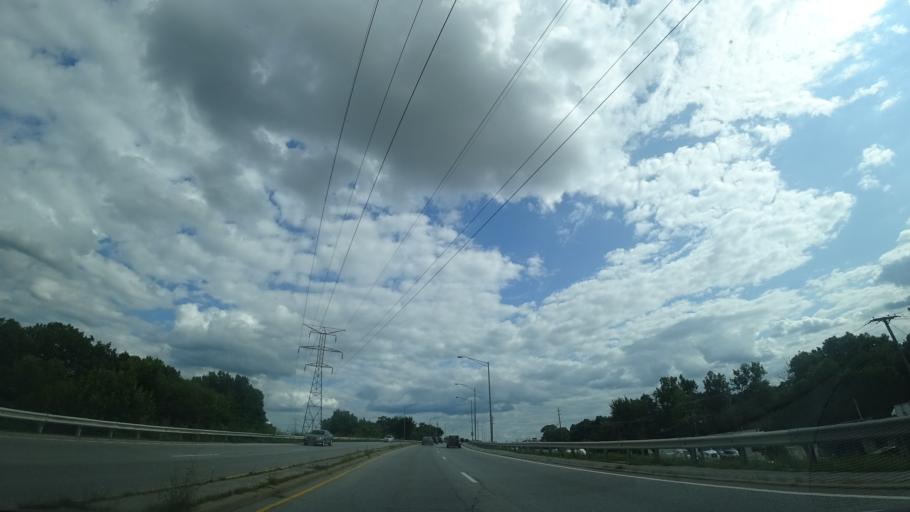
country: US
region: Illinois
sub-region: Cook County
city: Alsip
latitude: 41.6811
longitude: -87.7392
